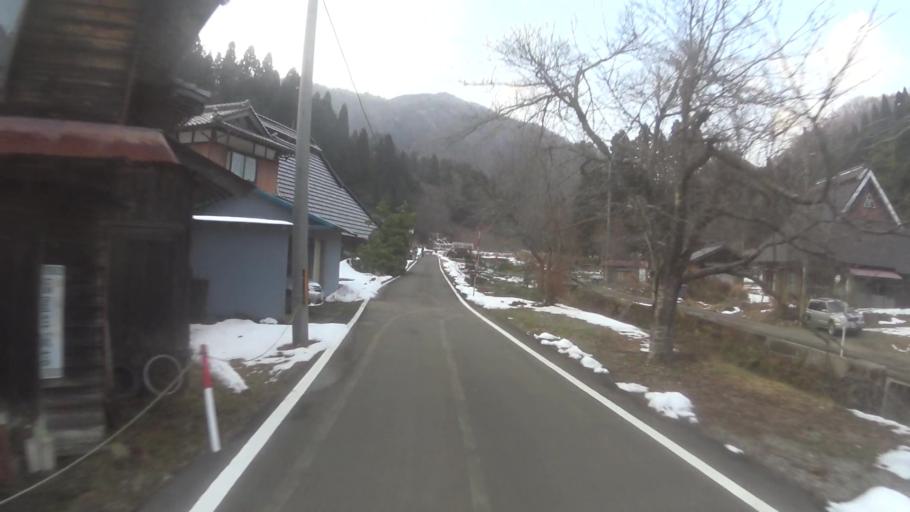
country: JP
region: Kyoto
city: Maizuru
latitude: 35.4367
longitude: 135.4726
